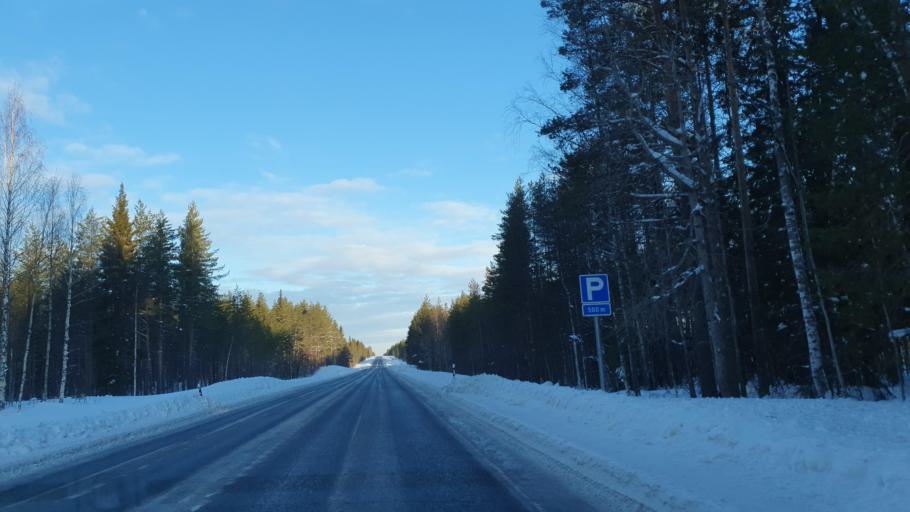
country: FI
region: Kainuu
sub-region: Kajaani
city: Vuolijoki
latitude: 64.4915
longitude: 27.3180
